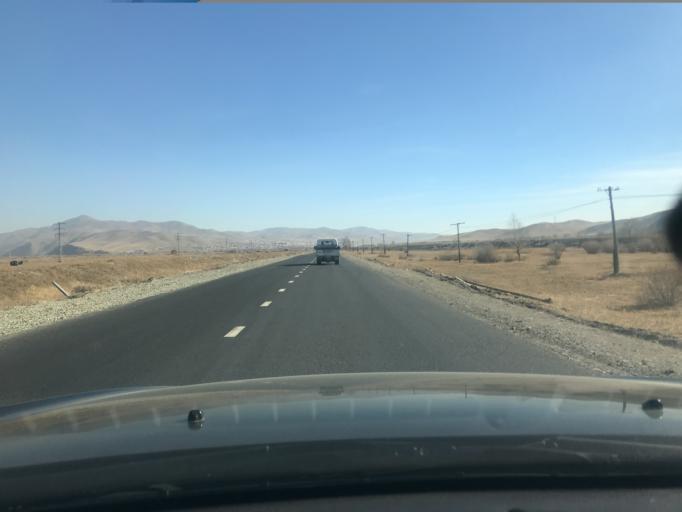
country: MN
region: Ulaanbaatar
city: Ulaanbaatar
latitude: 47.8986
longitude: 107.0413
